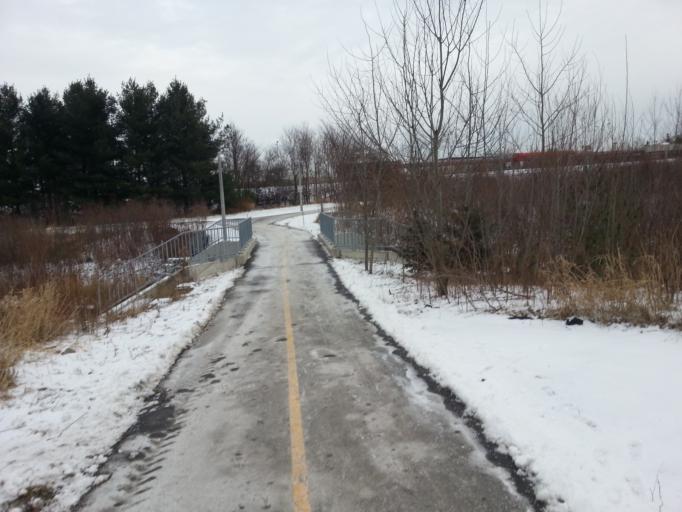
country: CA
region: Ontario
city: Ottawa
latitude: 45.3539
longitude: -75.6571
